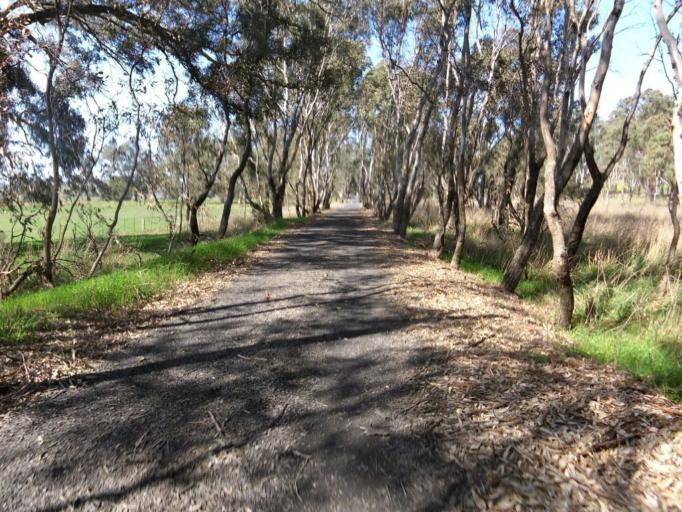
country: AU
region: Victoria
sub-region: Murrindindi
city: Alexandra
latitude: -37.0143
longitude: 145.7783
